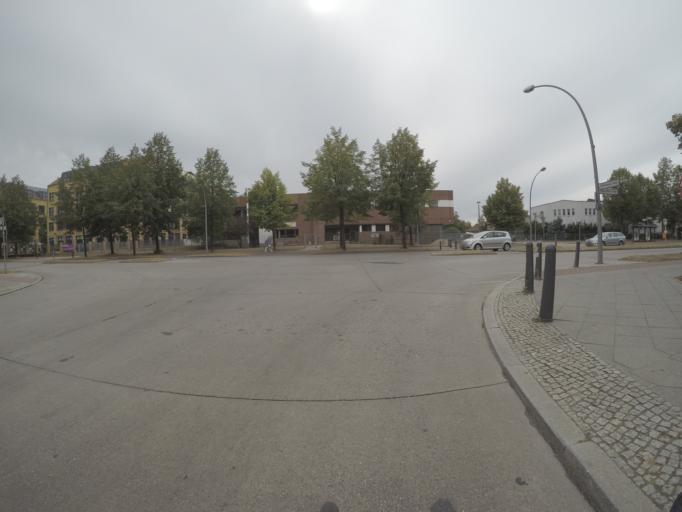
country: DE
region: Berlin
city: Alt-Hohenschoenhausen
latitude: 52.5465
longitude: 13.5118
